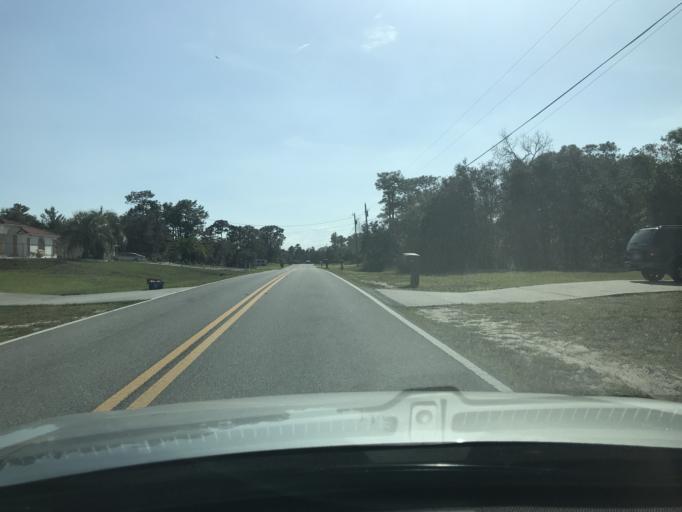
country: US
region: Florida
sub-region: Hernando County
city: North Weeki Wachee
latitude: 28.5426
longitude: -82.5529
